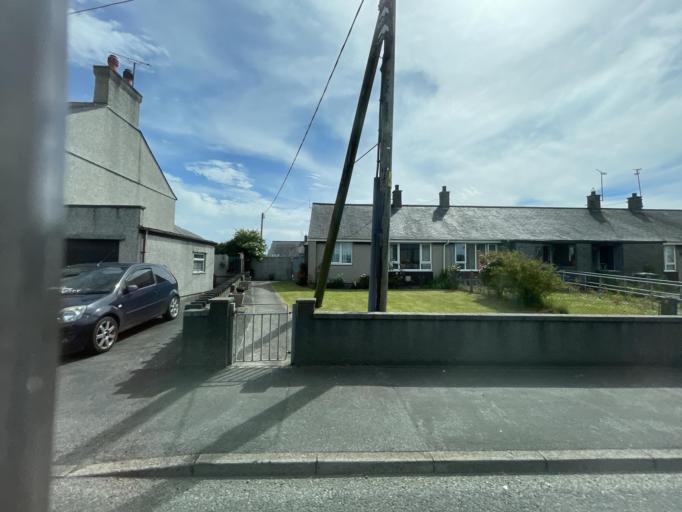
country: GB
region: Wales
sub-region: Anglesey
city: Llanfachraeth
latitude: 53.2696
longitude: -4.4779
